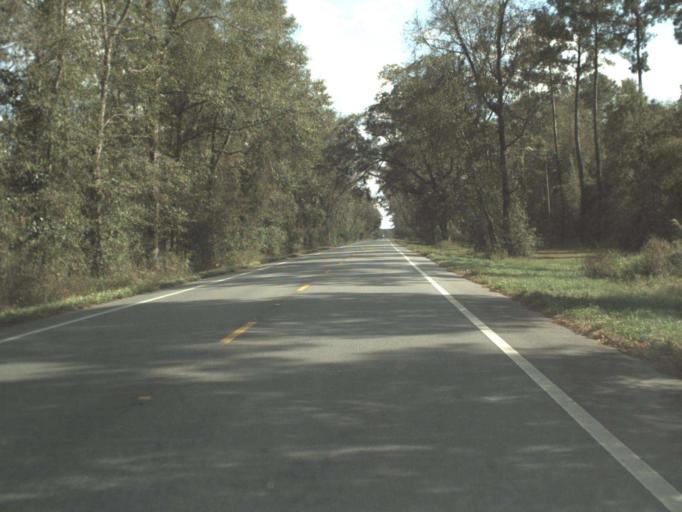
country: US
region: Florida
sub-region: Gadsden County
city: Gretna
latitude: 30.6855
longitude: -84.7175
